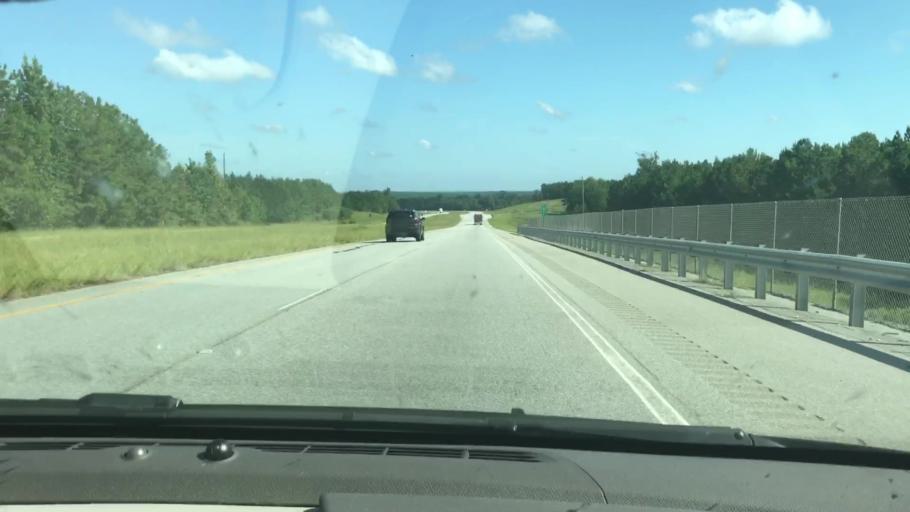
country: US
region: Alabama
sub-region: Barbour County
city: Eufaula
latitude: 32.1610
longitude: -85.1777
